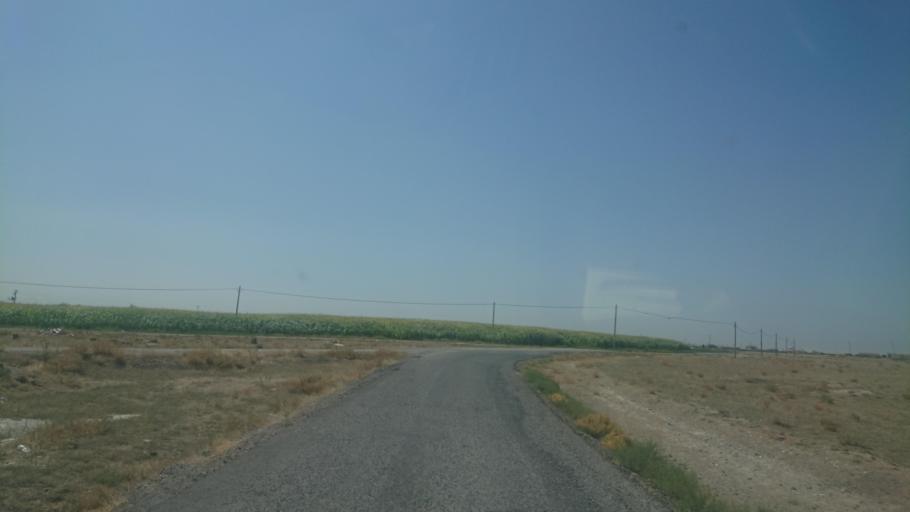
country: TR
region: Aksaray
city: Yesilova
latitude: 38.2960
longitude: 33.7279
